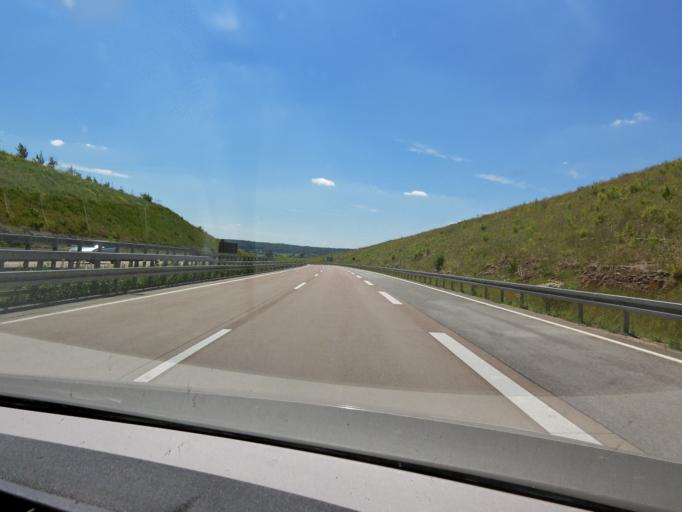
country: DE
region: Thuringia
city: Bretleben
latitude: 51.3225
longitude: 11.2421
